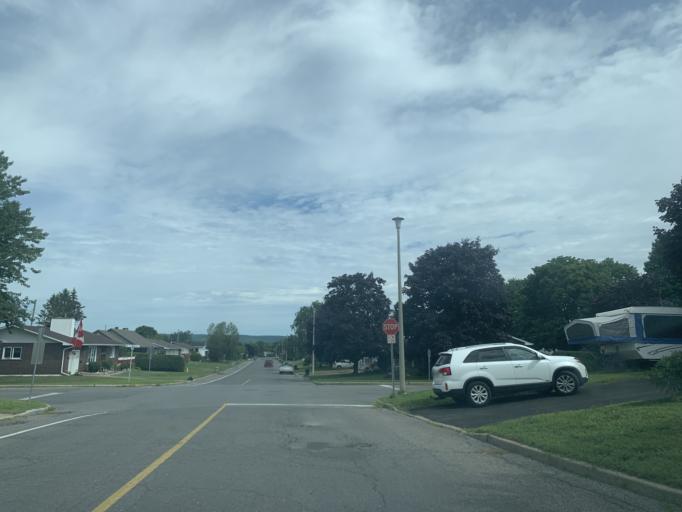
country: CA
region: Ontario
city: Hawkesbury
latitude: 45.5992
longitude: -74.6032
